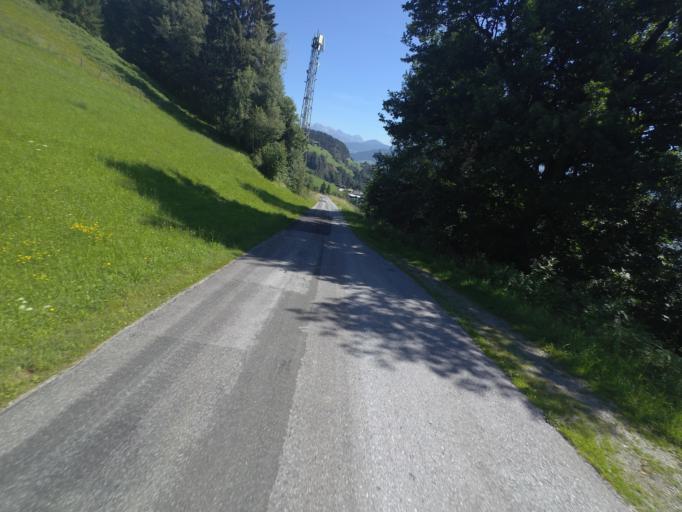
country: AT
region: Salzburg
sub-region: Politischer Bezirk Sankt Johann im Pongau
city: Sankt Johann im Pongau
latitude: 47.3556
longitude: 13.1862
